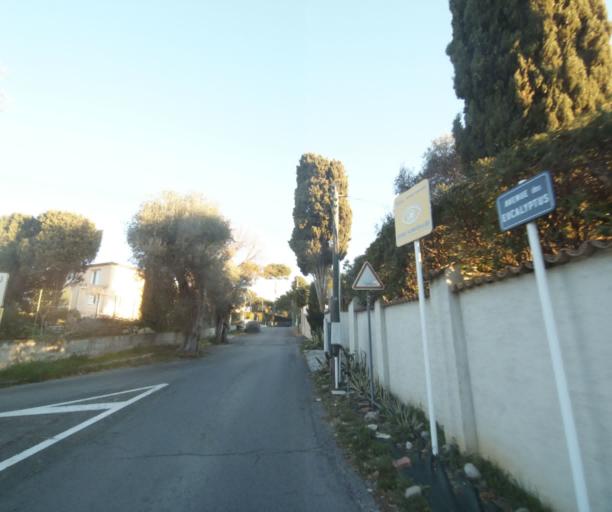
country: FR
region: Provence-Alpes-Cote d'Azur
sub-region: Departement des Alpes-Maritimes
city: Vallauris
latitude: 43.5795
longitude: 7.0846
